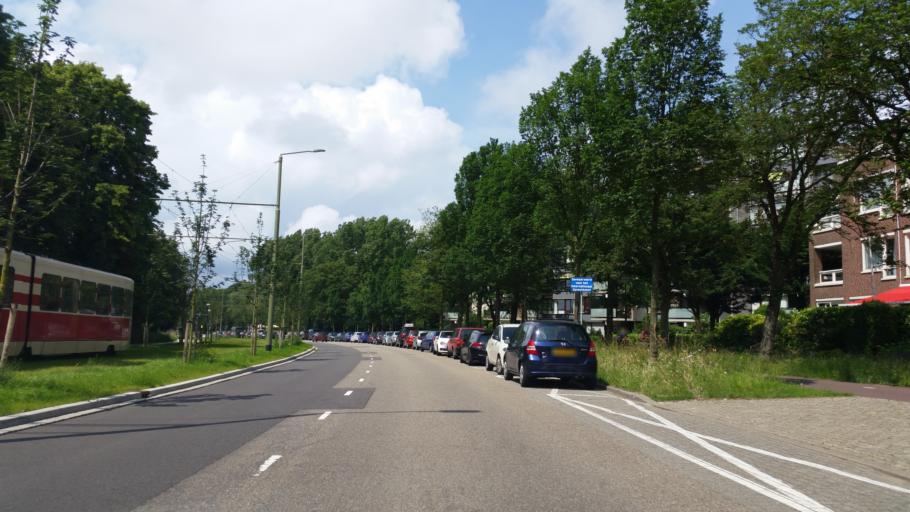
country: NL
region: South Holland
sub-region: Gemeente Den Haag
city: Scheveningen
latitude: 52.1039
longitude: 4.2960
